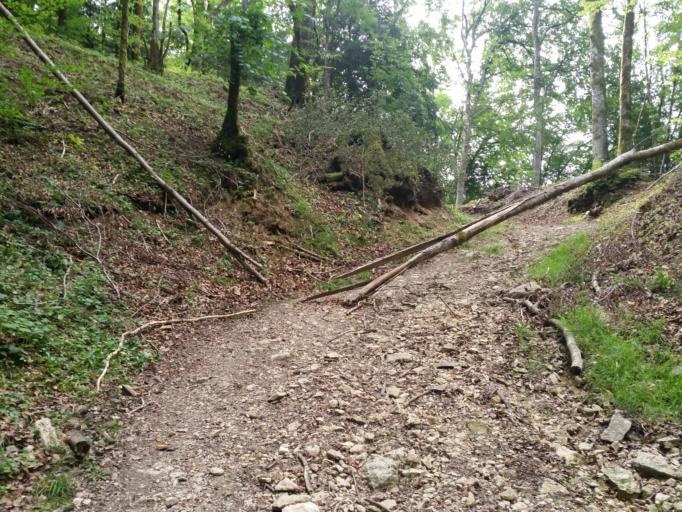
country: FR
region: Franche-Comte
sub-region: Departement du Jura
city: Salins-les-Bains
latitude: 46.9676
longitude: 5.9967
